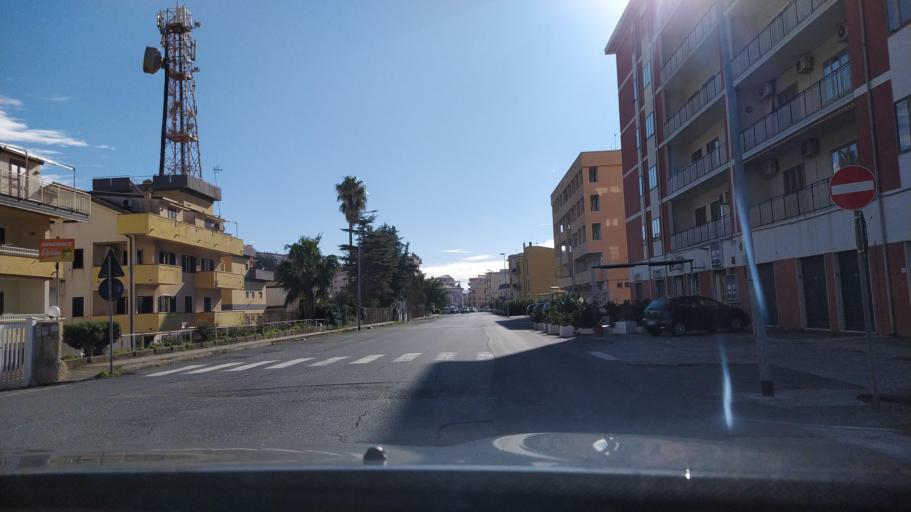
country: IT
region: Calabria
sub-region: Provincia di Cosenza
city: Paola
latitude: 39.3703
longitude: 16.0281
